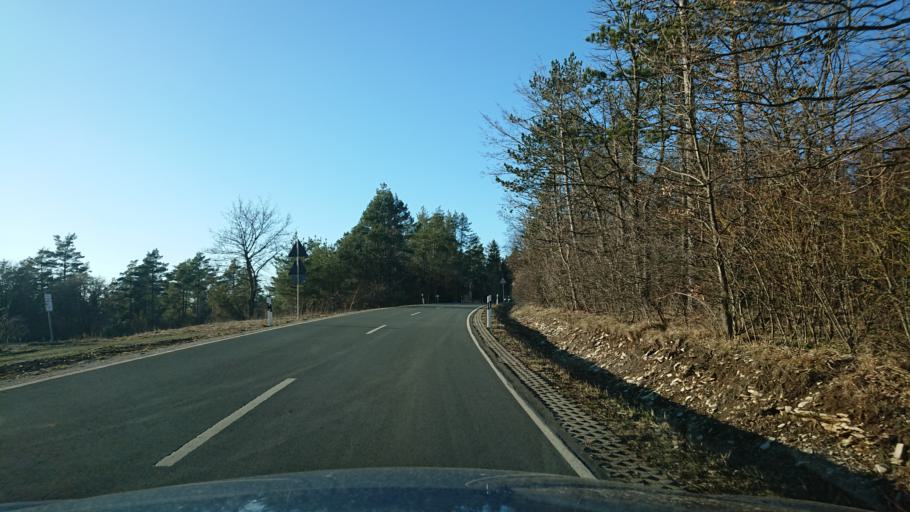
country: DE
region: Bavaria
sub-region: Upper Franconia
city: Ebermannstadt
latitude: 49.7828
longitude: 11.1623
